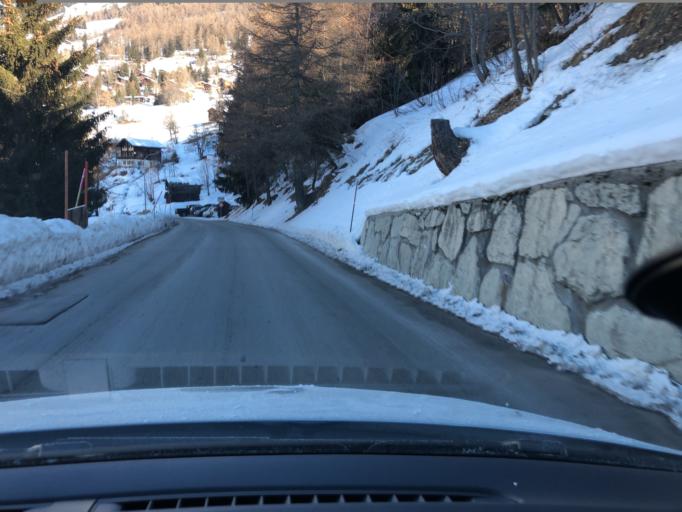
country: CH
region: Valais
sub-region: Goms District
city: Fiesch
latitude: 46.4263
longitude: 8.1583
